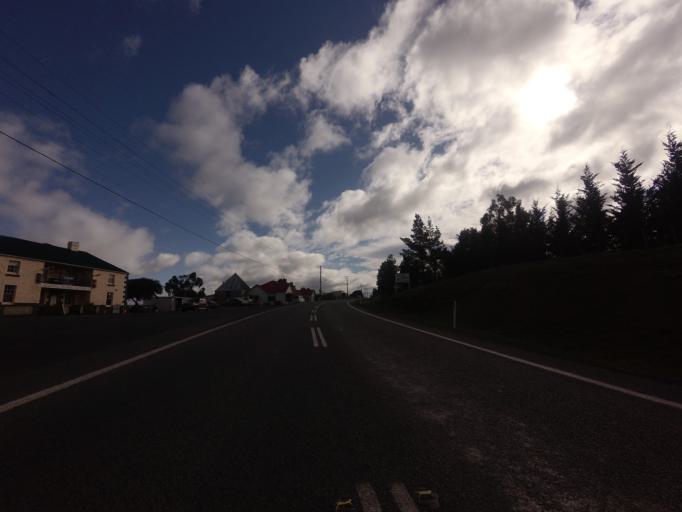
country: AU
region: Tasmania
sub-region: Derwent Valley
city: New Norfolk
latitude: -42.6817
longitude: 146.9382
